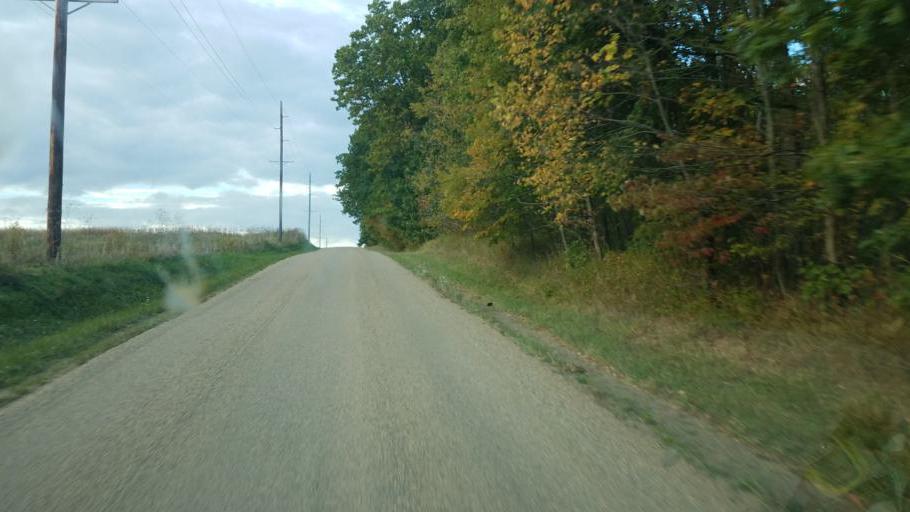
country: US
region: Ohio
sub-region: Ashland County
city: Loudonville
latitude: 40.6977
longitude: -82.2124
